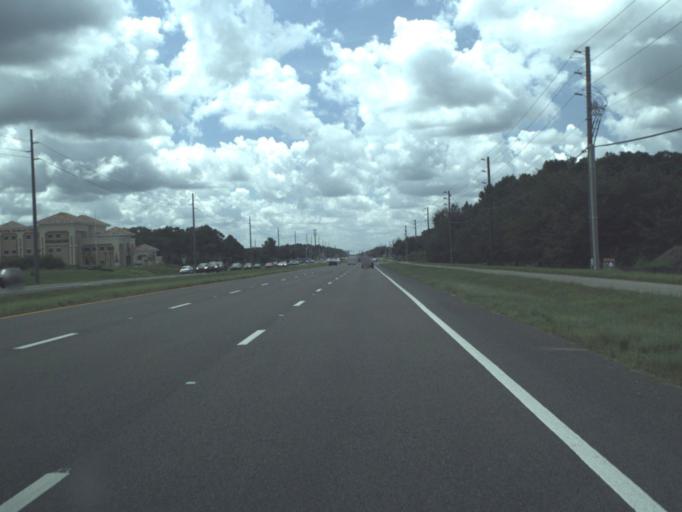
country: US
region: Florida
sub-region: Hillsborough County
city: Pebble Creek
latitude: 28.1932
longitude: -82.3537
